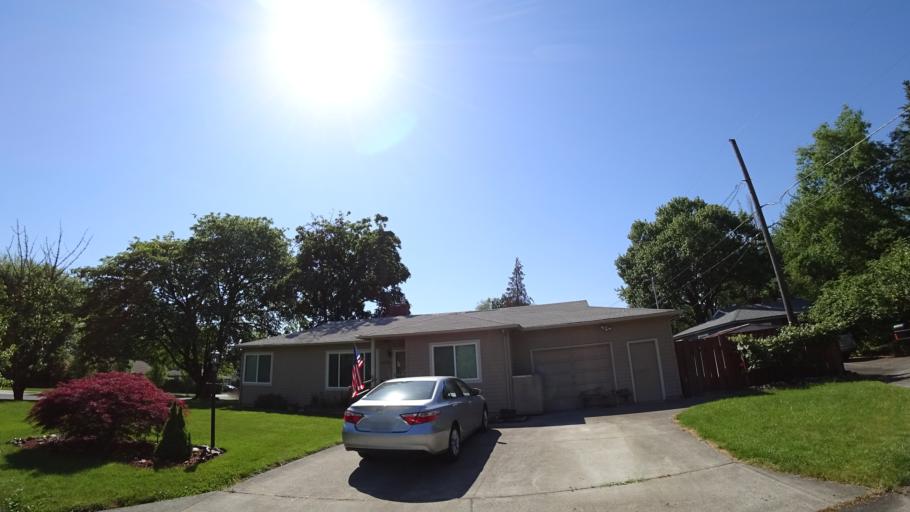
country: US
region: Oregon
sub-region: Washington County
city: Cedar Hills
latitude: 45.4974
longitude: -122.8054
